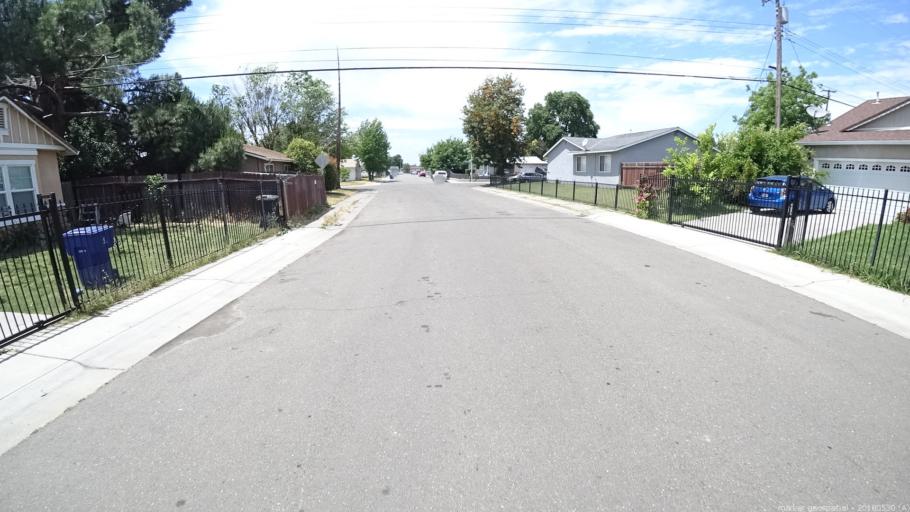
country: US
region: California
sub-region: Sacramento County
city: Sacramento
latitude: 38.6267
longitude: -121.4655
